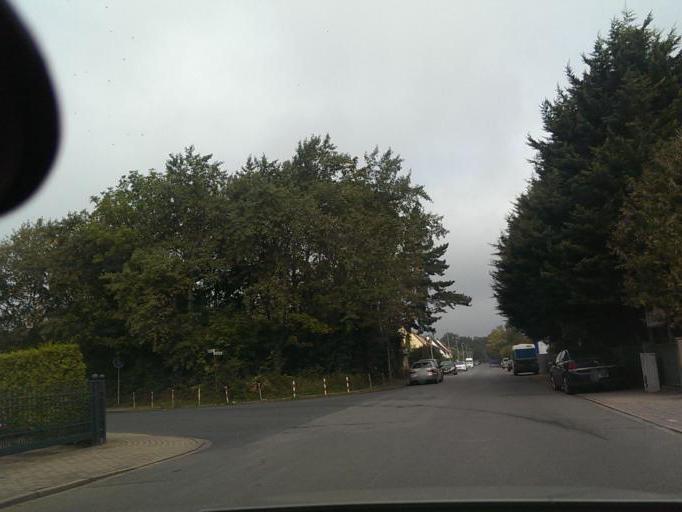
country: DE
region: Lower Saxony
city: Isernhagen Farster Bauerschaft
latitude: 52.4268
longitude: 9.8383
